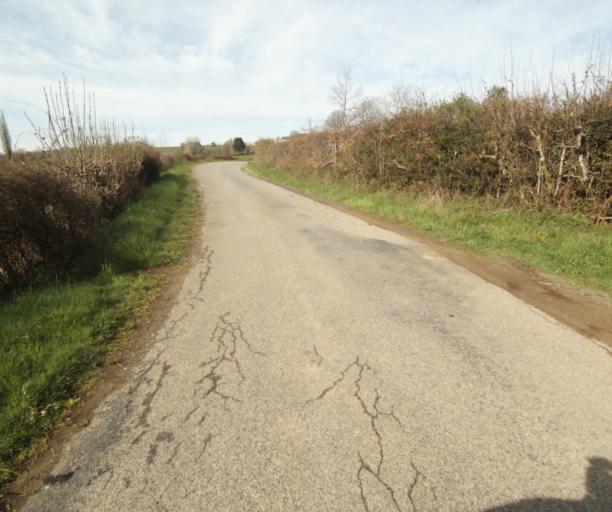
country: FR
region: Limousin
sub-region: Departement de la Correze
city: Laguenne
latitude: 45.2718
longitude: 1.8225
